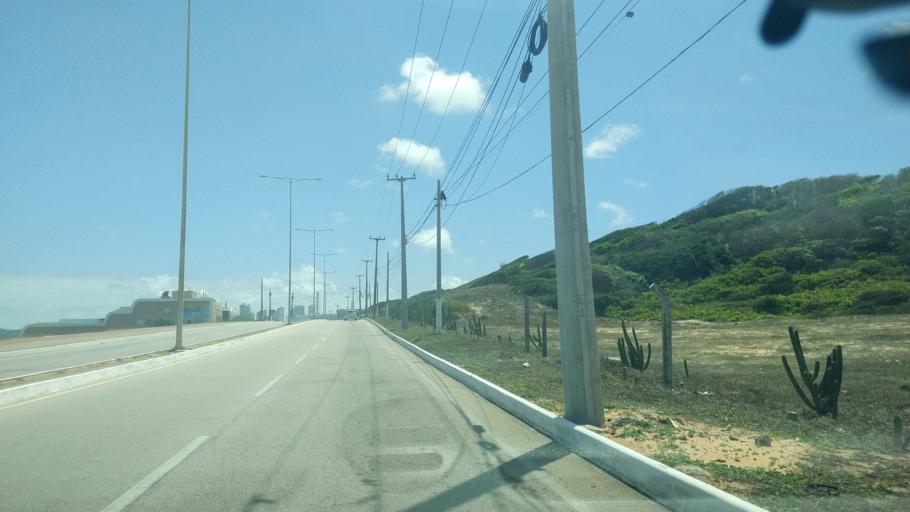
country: BR
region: Rio Grande do Norte
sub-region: Natal
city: Natal
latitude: -5.8524
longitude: -35.1823
